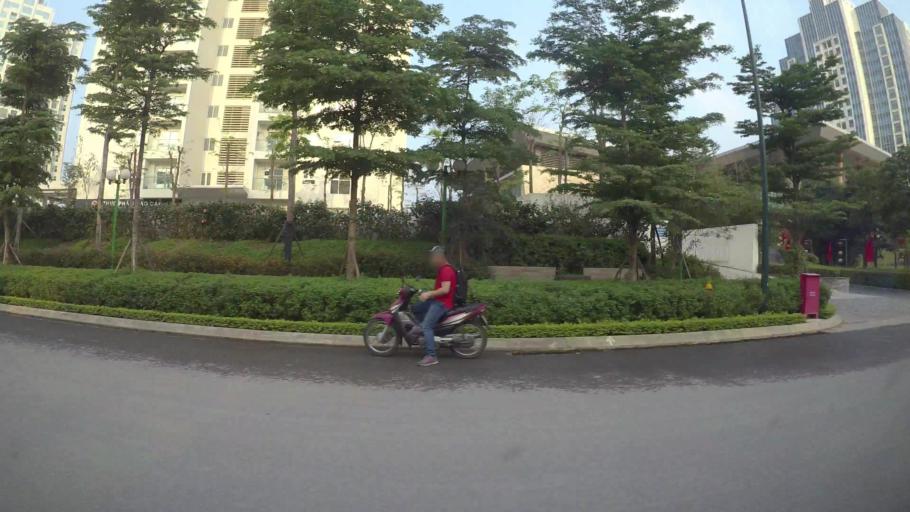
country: VN
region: Ha Noi
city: Tay Ho
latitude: 21.0816
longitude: 105.7910
